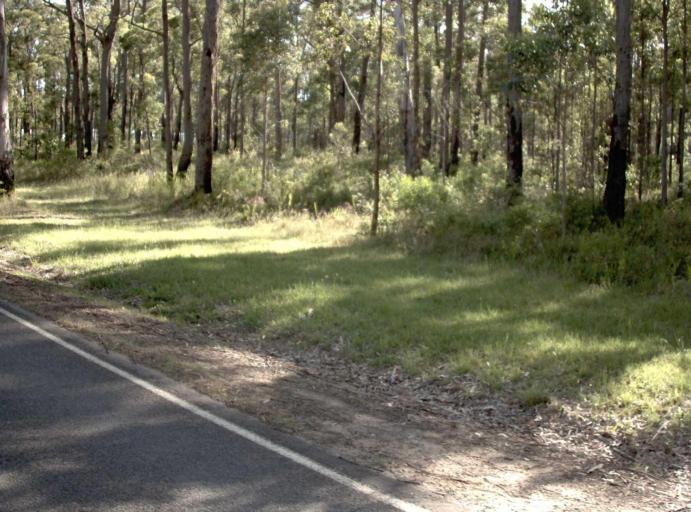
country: AU
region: Victoria
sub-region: East Gippsland
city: Lakes Entrance
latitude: -37.6795
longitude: 148.4712
